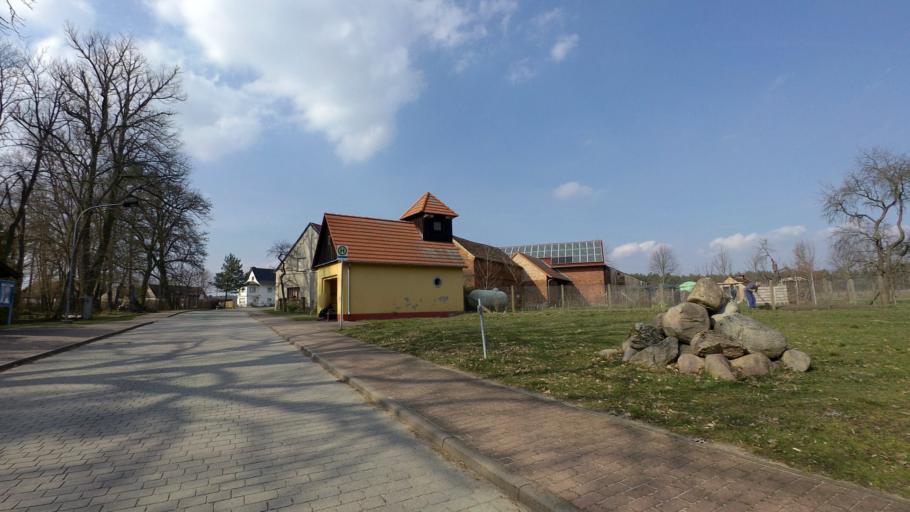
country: DE
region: Brandenburg
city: Dahme
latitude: 51.9414
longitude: 13.4436
